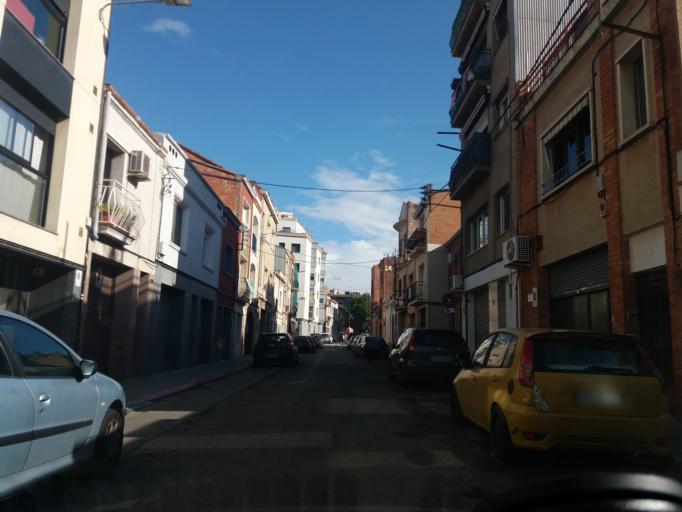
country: ES
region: Catalonia
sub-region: Provincia de Barcelona
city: Sabadell
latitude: 41.5574
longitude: 2.1009
